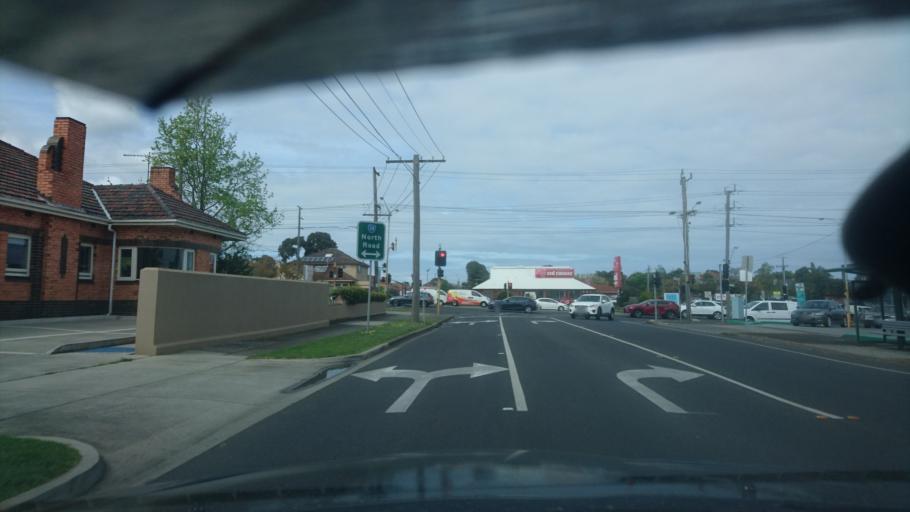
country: AU
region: Victoria
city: McKinnon
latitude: -37.9052
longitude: 145.0541
